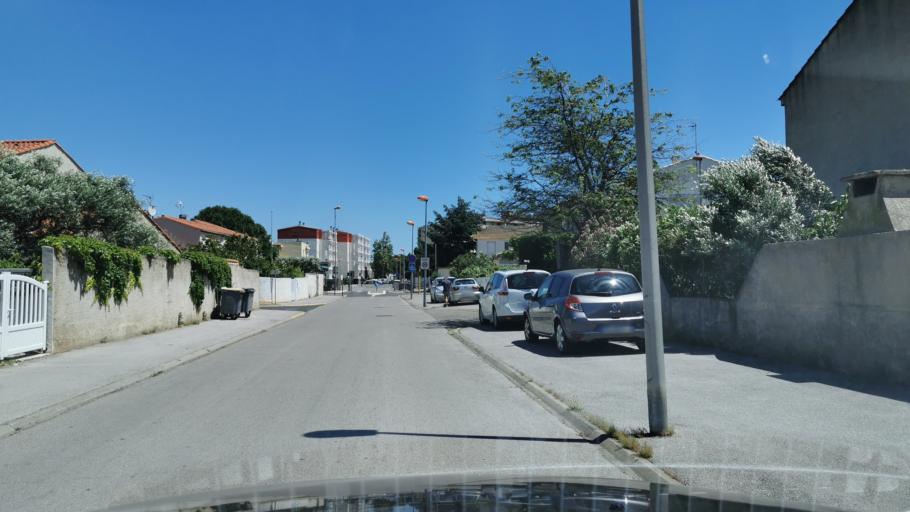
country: FR
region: Languedoc-Roussillon
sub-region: Departement de l'Aude
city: Narbonne
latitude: 43.1827
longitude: 2.9771
